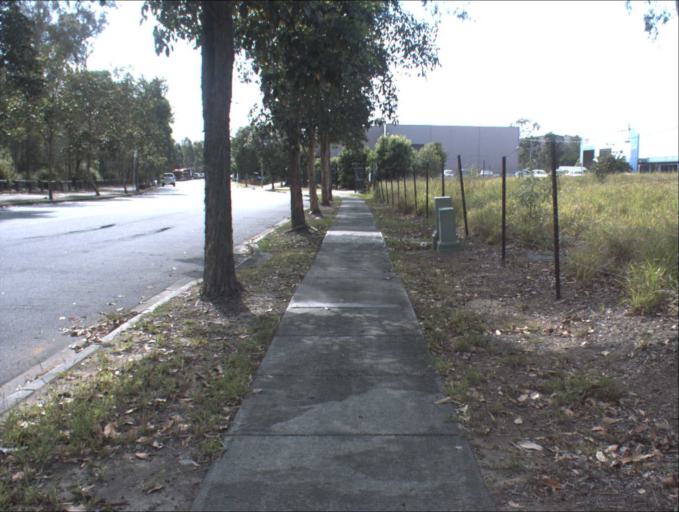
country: AU
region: Queensland
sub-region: Logan
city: Woodridge
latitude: -27.6177
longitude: 153.1070
